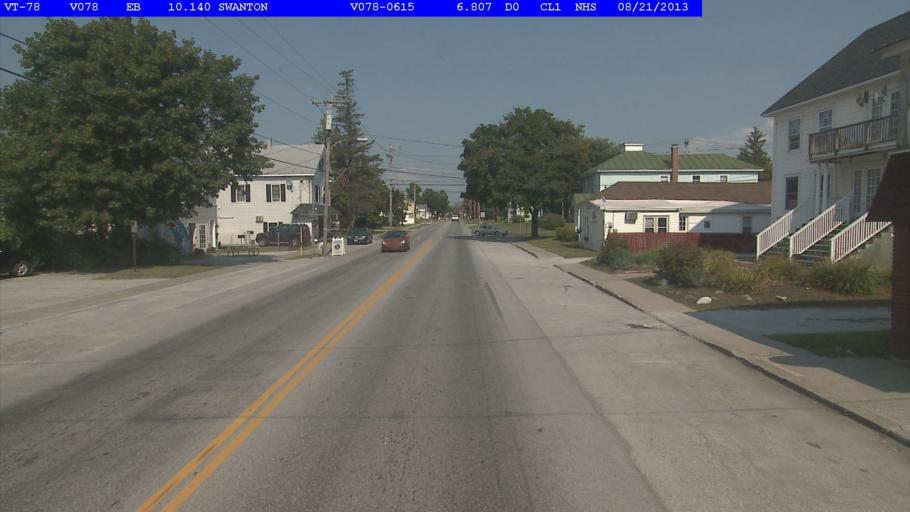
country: US
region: Vermont
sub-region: Franklin County
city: Swanton
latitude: 44.9184
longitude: -73.1238
